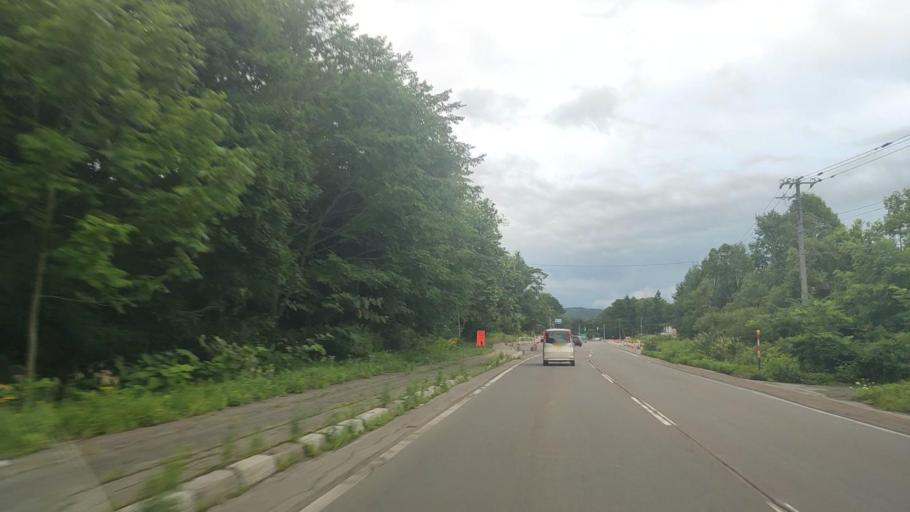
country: JP
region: Hokkaido
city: Nanae
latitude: 41.9973
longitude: 140.6359
